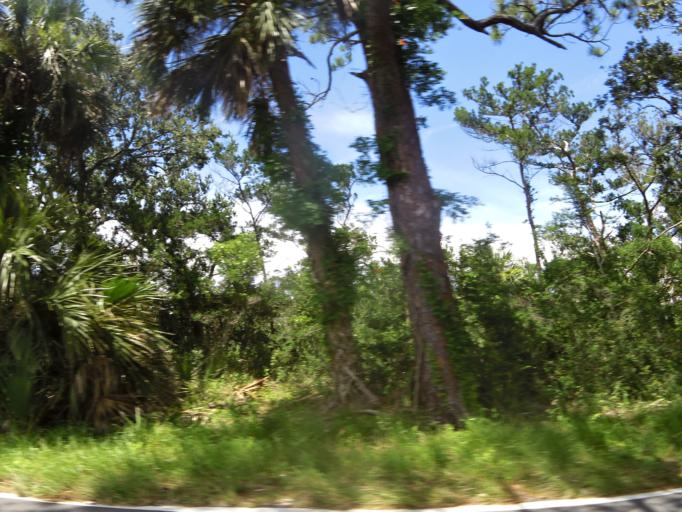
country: US
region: Florida
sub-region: Volusia County
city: Ormond-by-the-Sea
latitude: 29.3538
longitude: -81.1038
